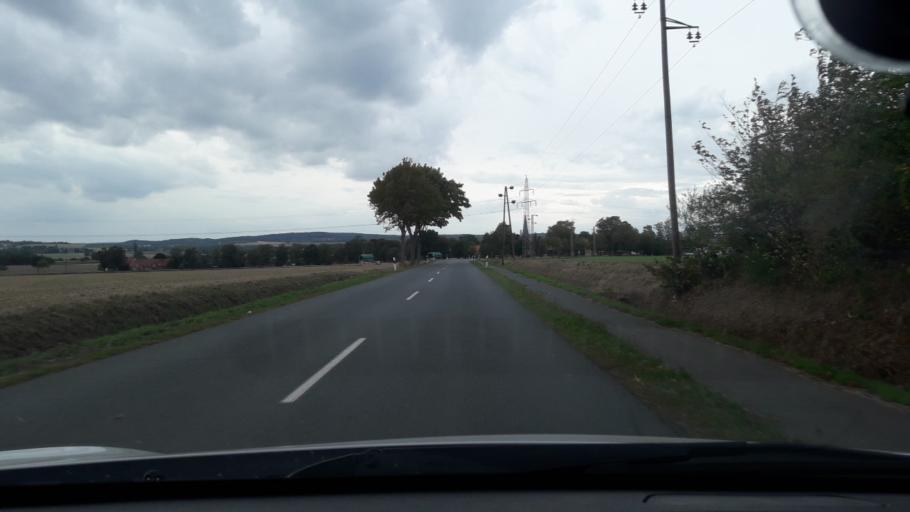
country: DE
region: Lower Saxony
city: Flothe
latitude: 52.0599
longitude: 10.4556
